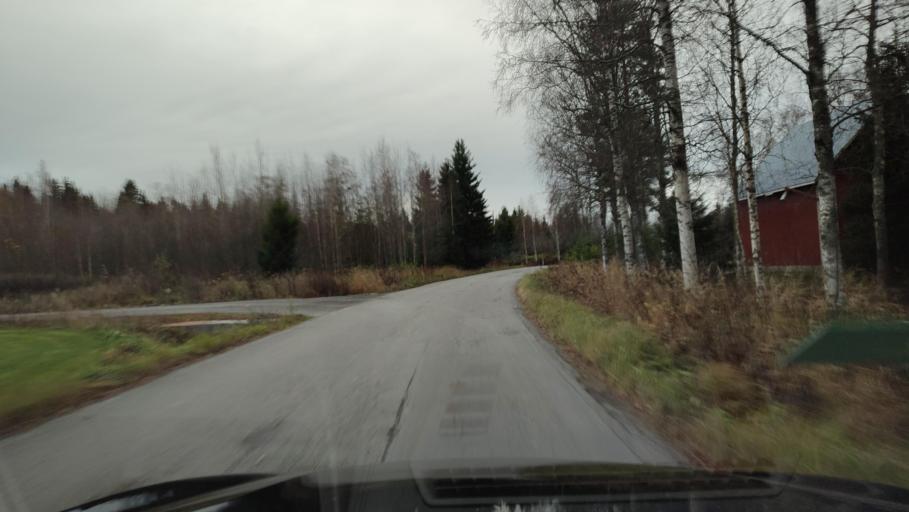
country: FI
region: Ostrobothnia
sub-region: Sydosterbotten
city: Naerpes
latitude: 62.4271
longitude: 21.4174
